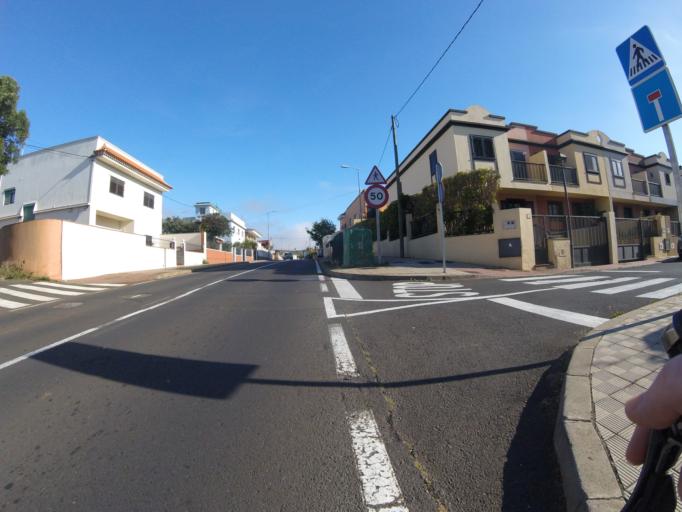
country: ES
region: Canary Islands
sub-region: Provincia de Santa Cruz de Tenerife
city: La Laguna
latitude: 28.4613
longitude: -16.3154
